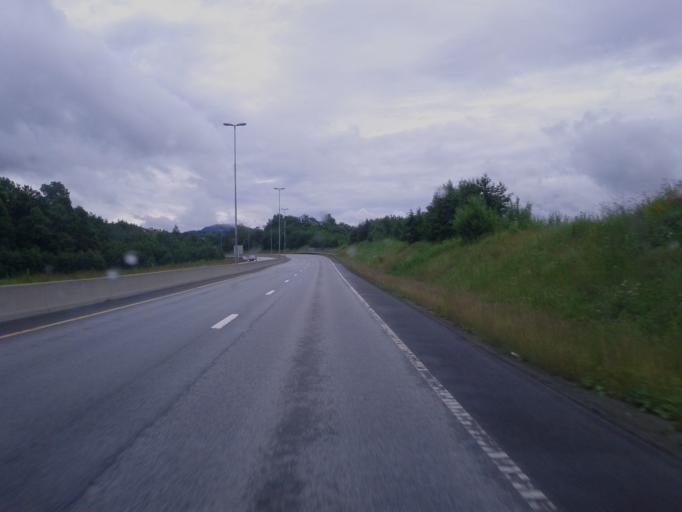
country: NO
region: Sor-Trondelag
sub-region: Melhus
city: Melhus
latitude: 63.2939
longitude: 10.2764
